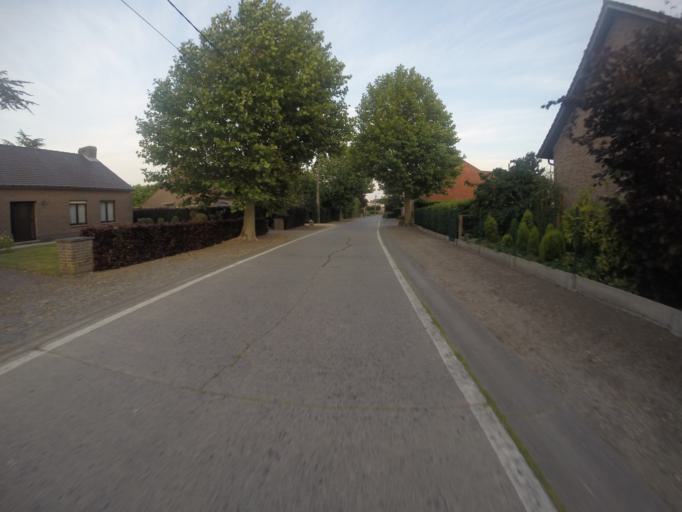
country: BE
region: Flanders
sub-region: Provincie Oost-Vlaanderen
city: Zomergem
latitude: 51.1169
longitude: 3.5412
